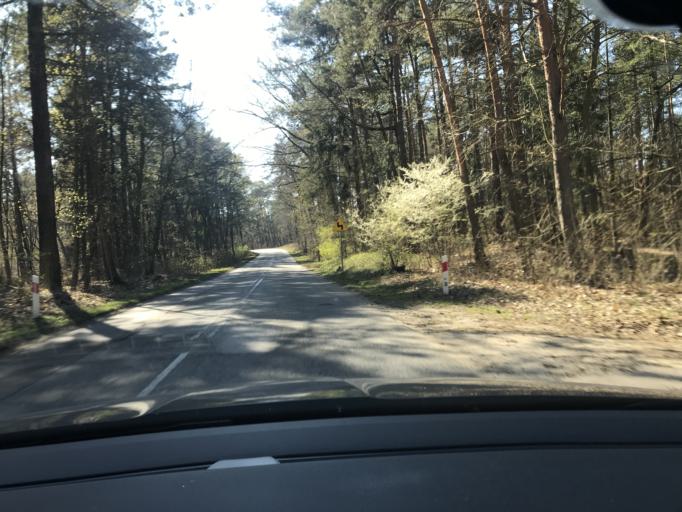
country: PL
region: Pomeranian Voivodeship
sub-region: Powiat nowodworski
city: Sztutowo
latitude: 54.3346
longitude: 19.1957
